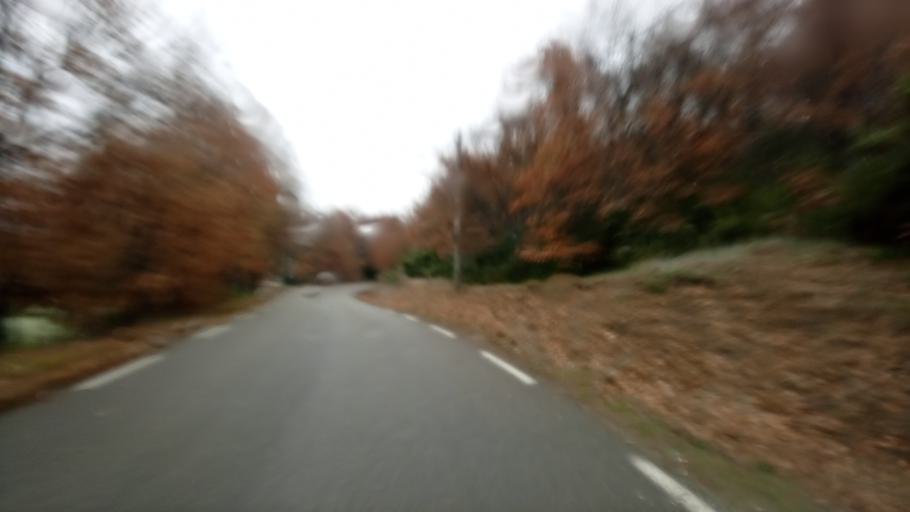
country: FR
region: Provence-Alpes-Cote d'Azur
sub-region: Departement du Var
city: Vinon-sur-Verdon
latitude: 43.7247
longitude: 5.8411
